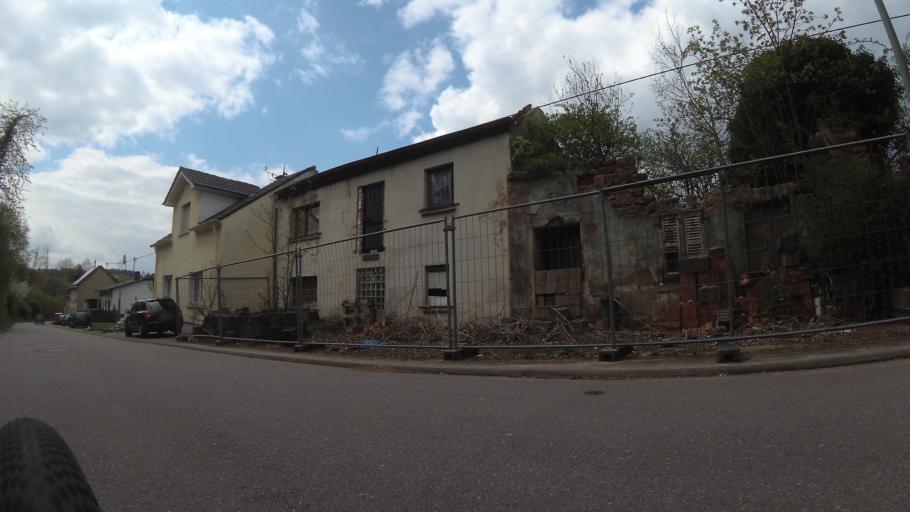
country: DE
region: Saarland
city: Schmelz
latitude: 49.4837
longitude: 6.8331
